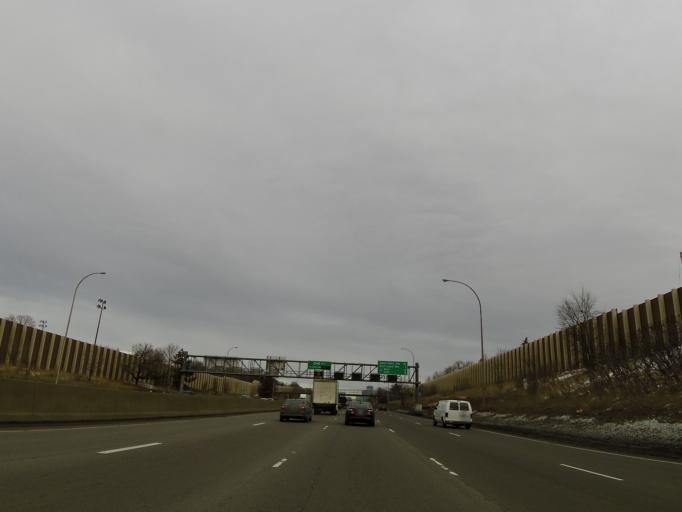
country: US
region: Minnesota
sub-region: Hennepin County
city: Richfield
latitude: 44.9282
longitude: -93.2746
